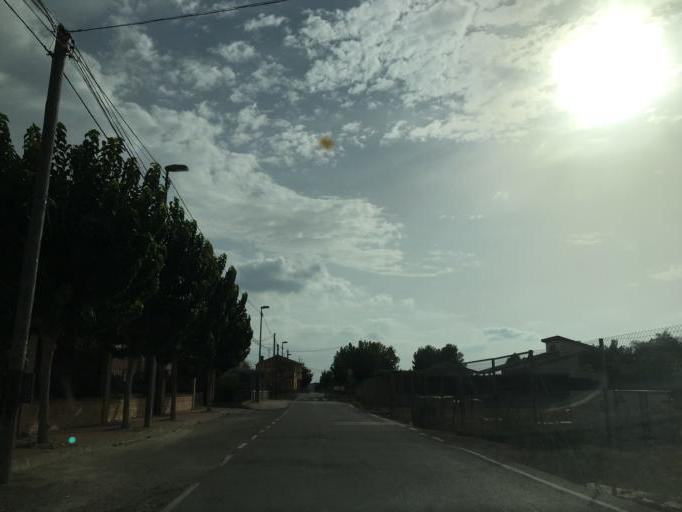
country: ES
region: Murcia
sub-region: Murcia
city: Murcia
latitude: 38.0185
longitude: -1.0895
